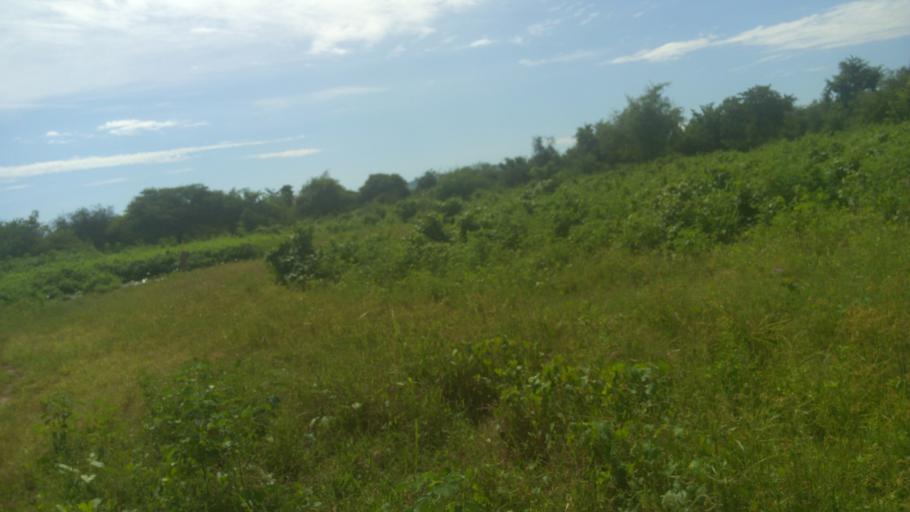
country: ML
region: Kayes
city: Yelimane
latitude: 14.8438
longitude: -10.7453
